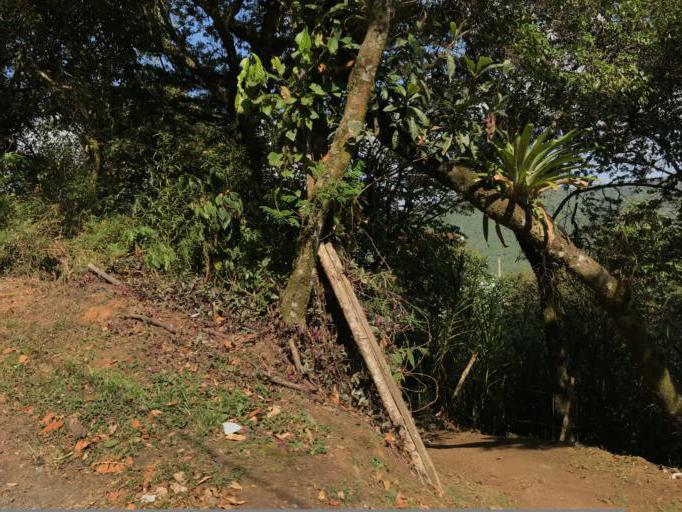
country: CO
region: Valle del Cauca
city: Cali
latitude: 3.4744
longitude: -76.6173
